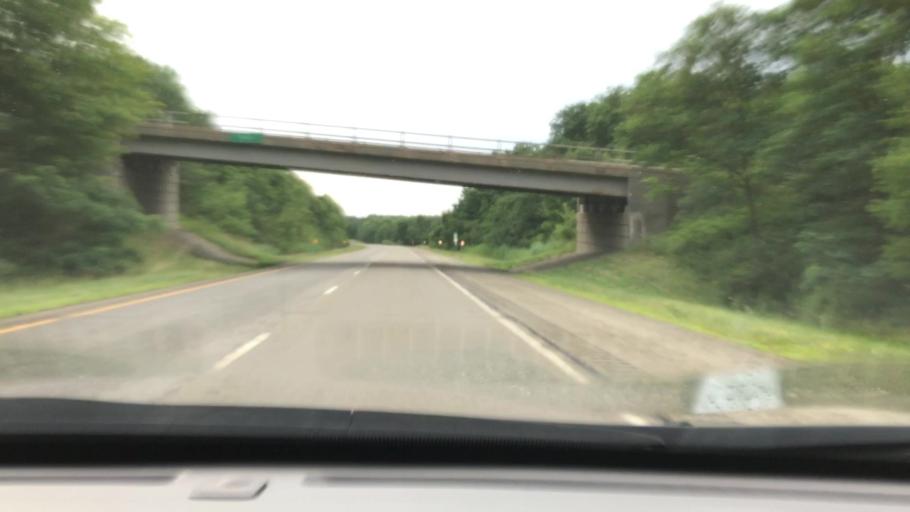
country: US
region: New York
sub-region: Erie County
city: North Boston
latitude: 42.6521
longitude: -78.7650
